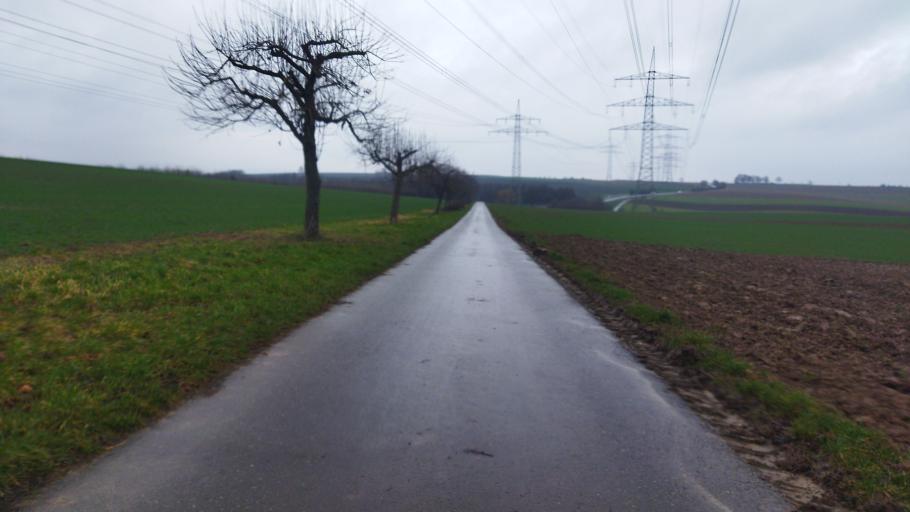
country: DE
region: Baden-Wuerttemberg
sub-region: Regierungsbezirk Stuttgart
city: Neckarwestheim
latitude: 49.0525
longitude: 9.1991
